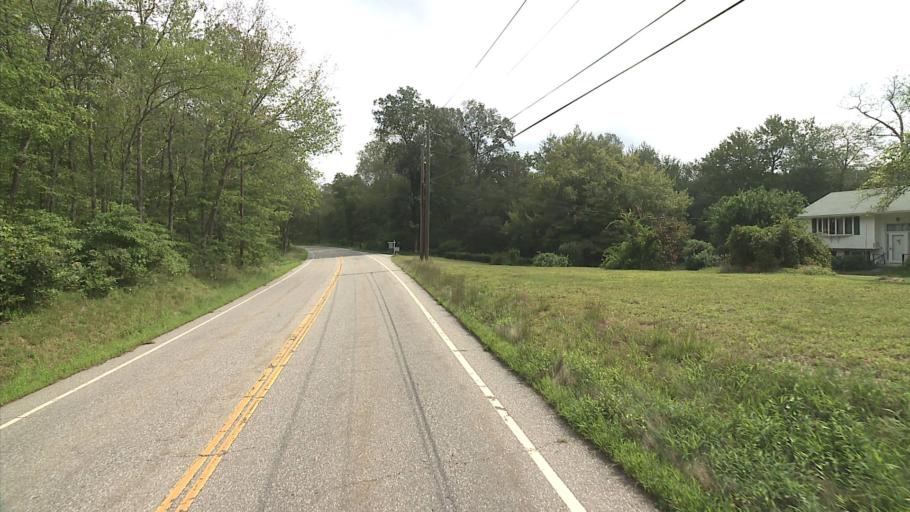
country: US
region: Connecticut
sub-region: New London County
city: Colchester
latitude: 41.4536
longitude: -72.3099
